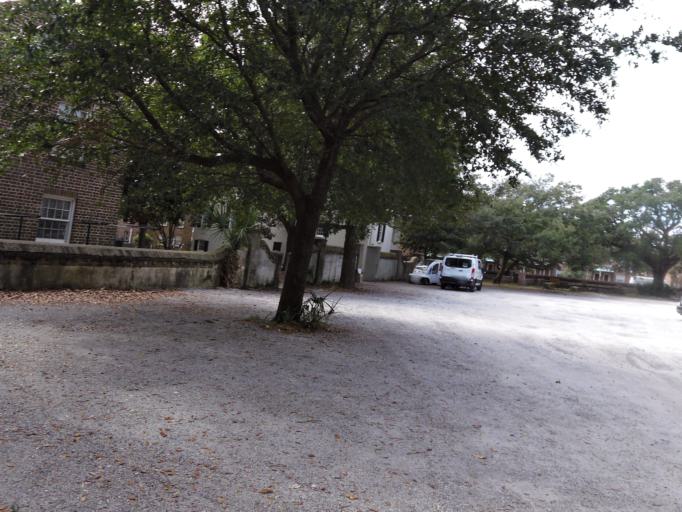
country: US
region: South Carolina
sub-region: Charleston County
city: Charleston
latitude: 32.7782
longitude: -79.9369
